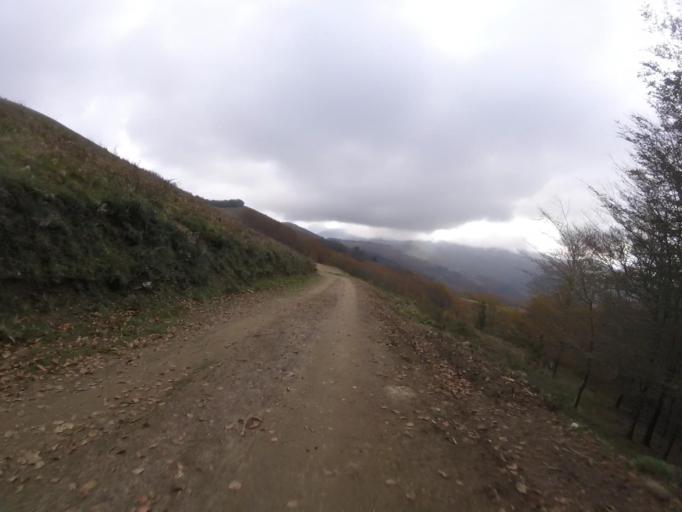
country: ES
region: Navarre
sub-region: Provincia de Navarra
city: Goizueta
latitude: 43.2009
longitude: -1.8308
